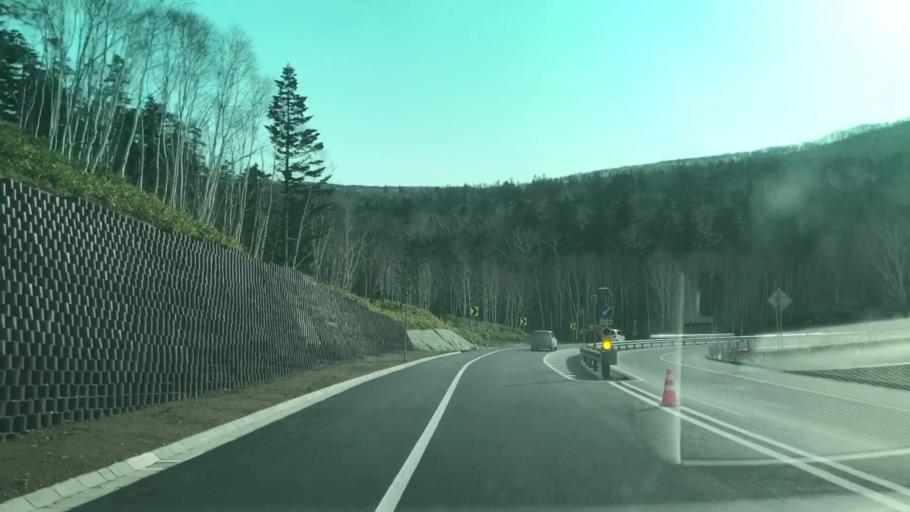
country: JP
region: Hokkaido
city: Otofuke
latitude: 42.9831
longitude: 142.7543
